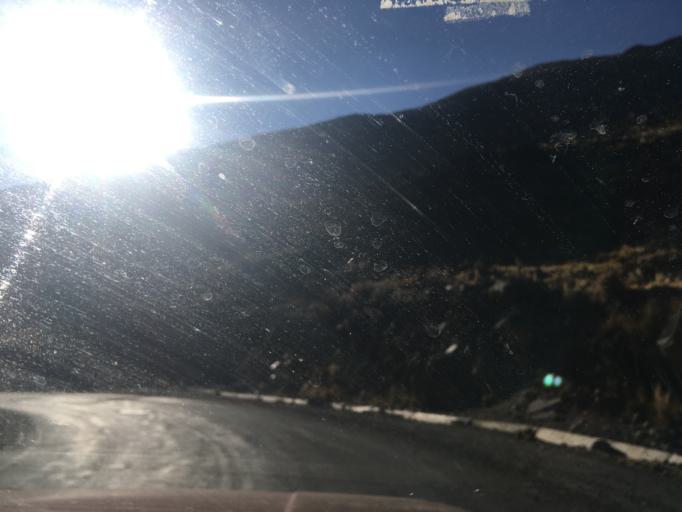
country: BO
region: La Paz
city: Quime
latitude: -17.0275
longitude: -67.2848
